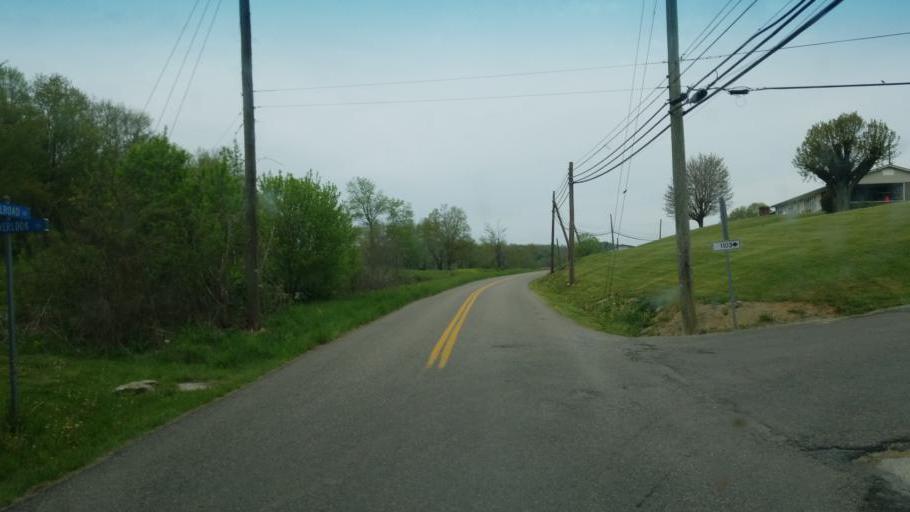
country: US
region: Virginia
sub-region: Smyth County
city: Adwolf
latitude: 36.8132
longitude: -81.5688
